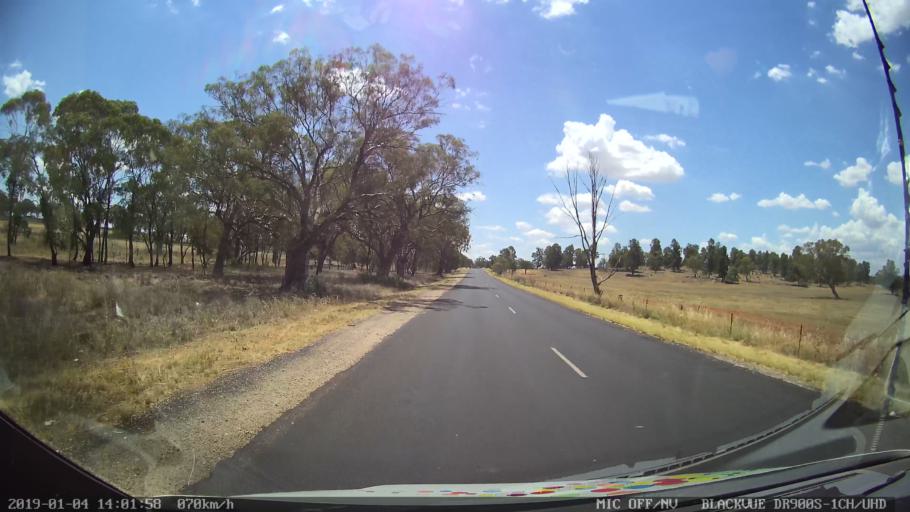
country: AU
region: New South Wales
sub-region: Dubbo Municipality
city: Dubbo
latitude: -32.2912
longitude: 148.5984
